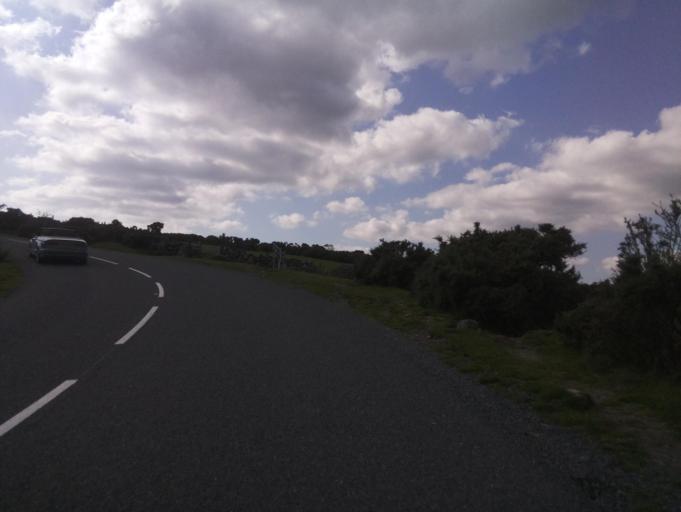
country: GB
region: England
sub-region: Devon
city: South Brent
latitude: 50.5557
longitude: -3.9163
